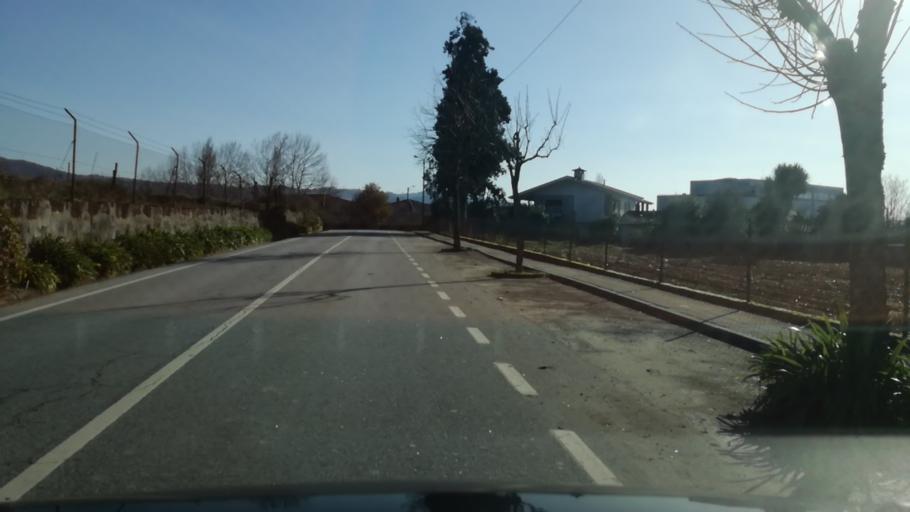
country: PT
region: Braga
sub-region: Guimaraes
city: Ponte
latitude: 41.5193
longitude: -8.3201
